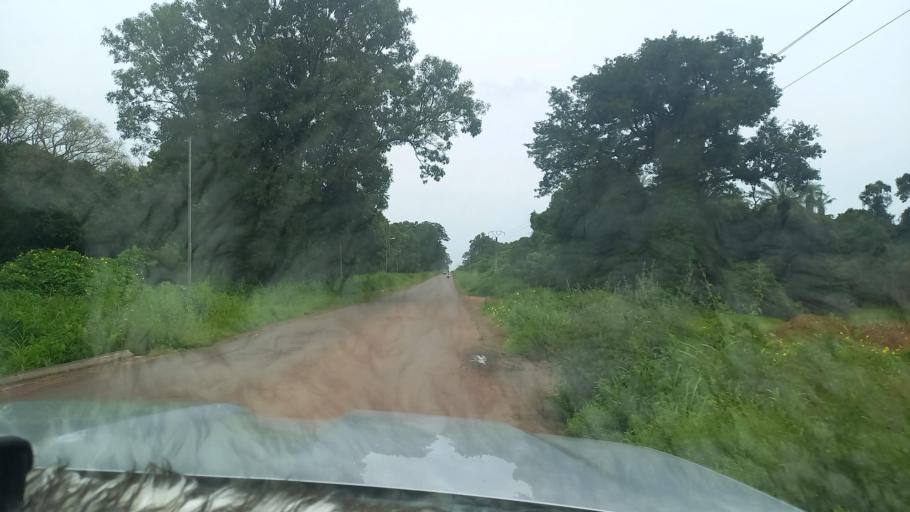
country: SN
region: Ziguinchor
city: Bignona
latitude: 12.8242
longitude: -16.1741
